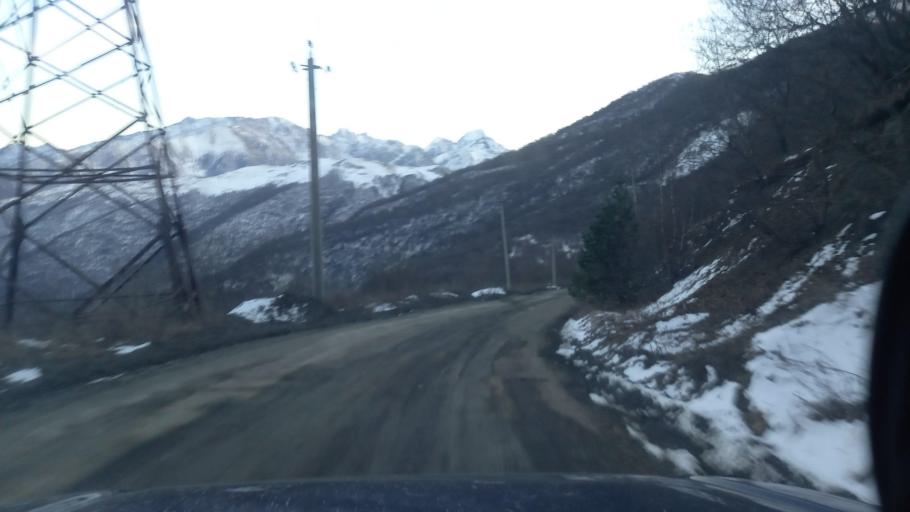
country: RU
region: Ingushetiya
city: Dzhayrakh
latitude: 42.8323
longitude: 44.5703
